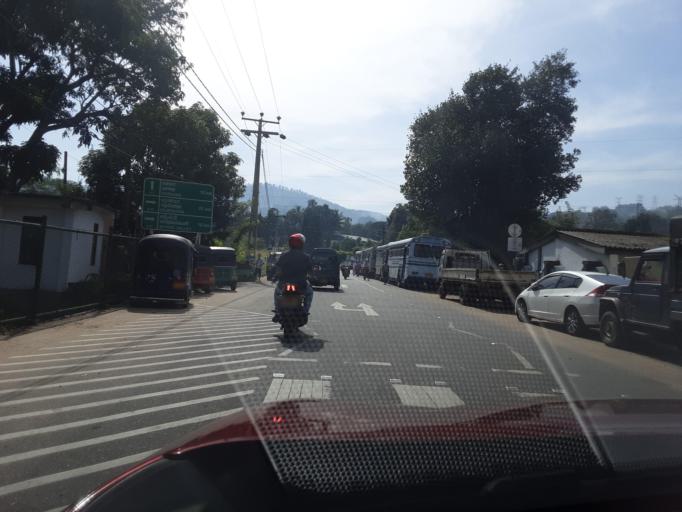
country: LK
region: Uva
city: Badulla
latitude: 6.9835
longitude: 81.0661
